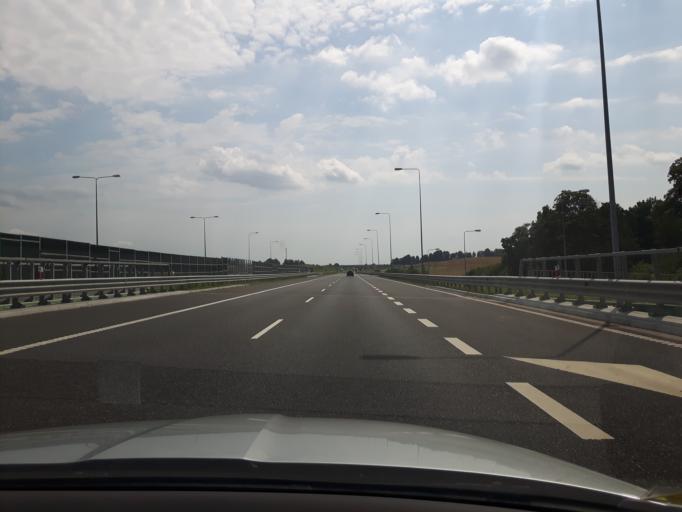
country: PL
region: Warmian-Masurian Voivodeship
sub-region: Powiat olsztynski
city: Olsztynek
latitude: 53.4976
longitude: 20.3140
